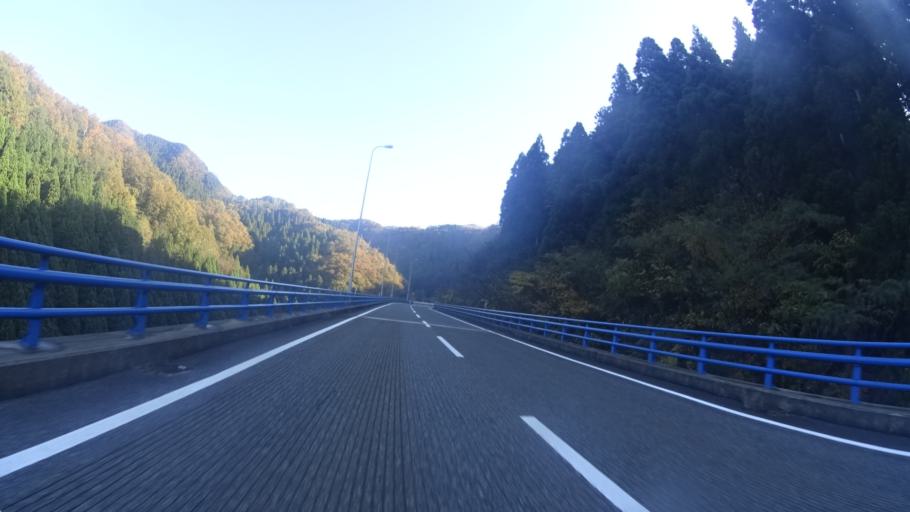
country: JP
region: Fukui
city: Maruoka
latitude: 36.1735
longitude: 136.3343
